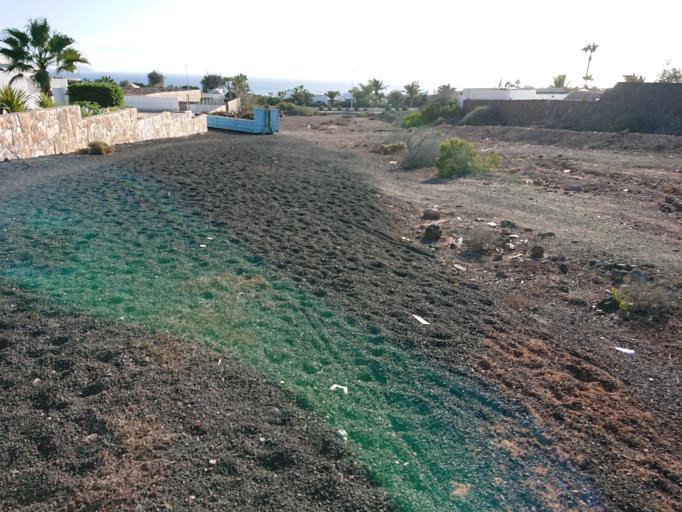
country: ES
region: Canary Islands
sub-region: Provincia de Las Palmas
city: Playa Blanca
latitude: 28.8666
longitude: -13.8479
